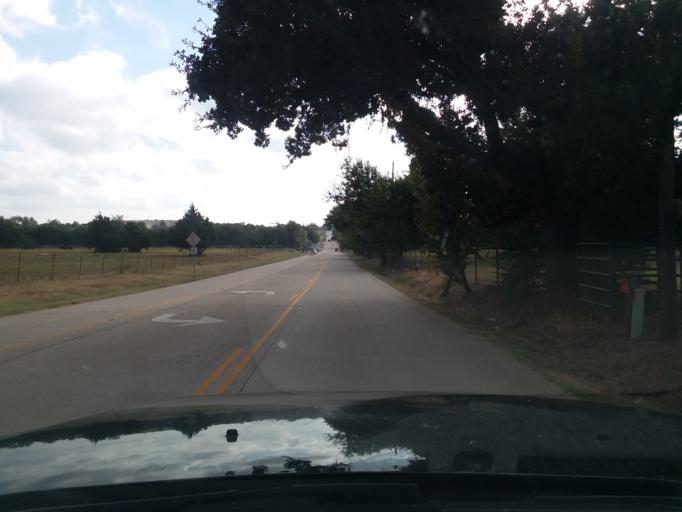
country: US
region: Texas
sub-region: Denton County
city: Hickory Creek
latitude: 33.1227
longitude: -97.0454
